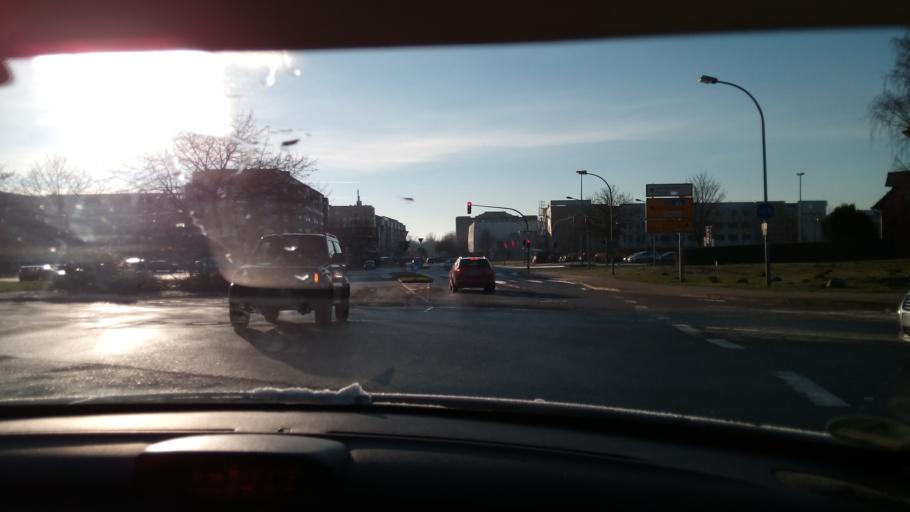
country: DE
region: Mecklenburg-Vorpommern
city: Neubrandenburg
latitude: 53.5577
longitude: 13.2480
